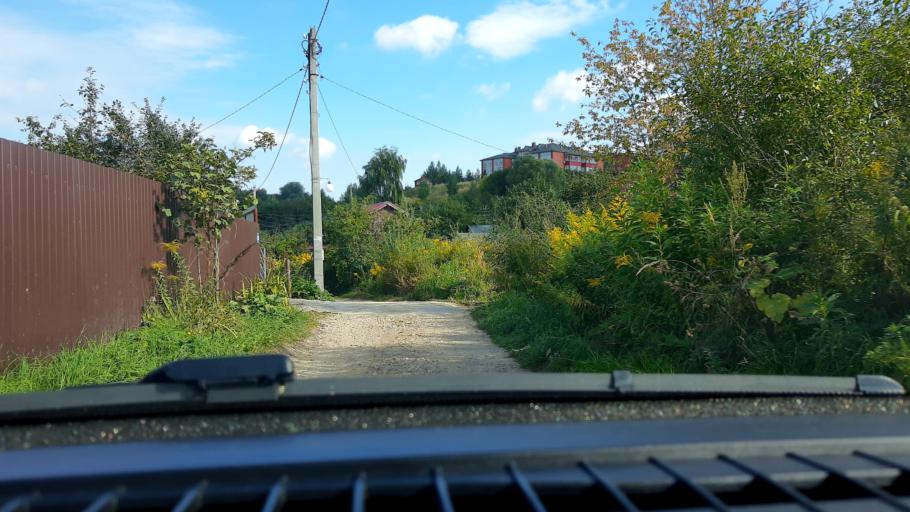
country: RU
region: Nizjnij Novgorod
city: Afonino
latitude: 56.2620
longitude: 44.0874
